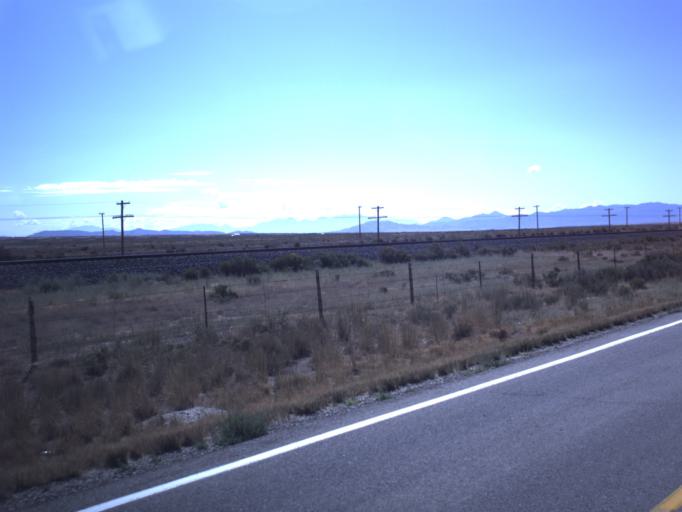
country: US
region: Utah
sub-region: Tooele County
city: Tooele
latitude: 40.3163
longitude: -112.4056
